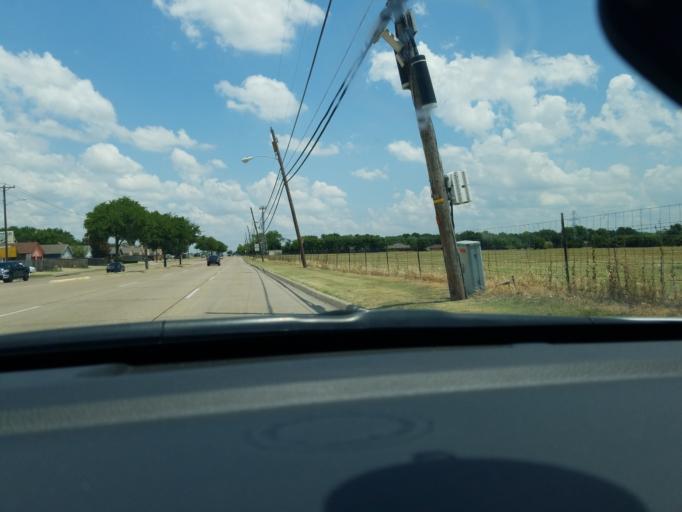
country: US
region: Texas
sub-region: Dallas County
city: Sunnyvale
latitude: 32.8172
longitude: -96.5958
